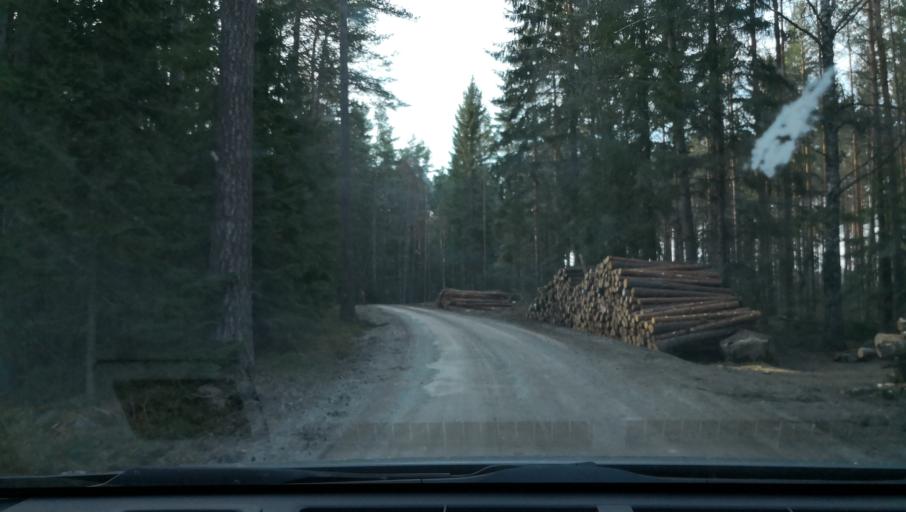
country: SE
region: OErebro
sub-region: Lindesbergs Kommun
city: Frovi
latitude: 59.3552
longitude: 15.3364
